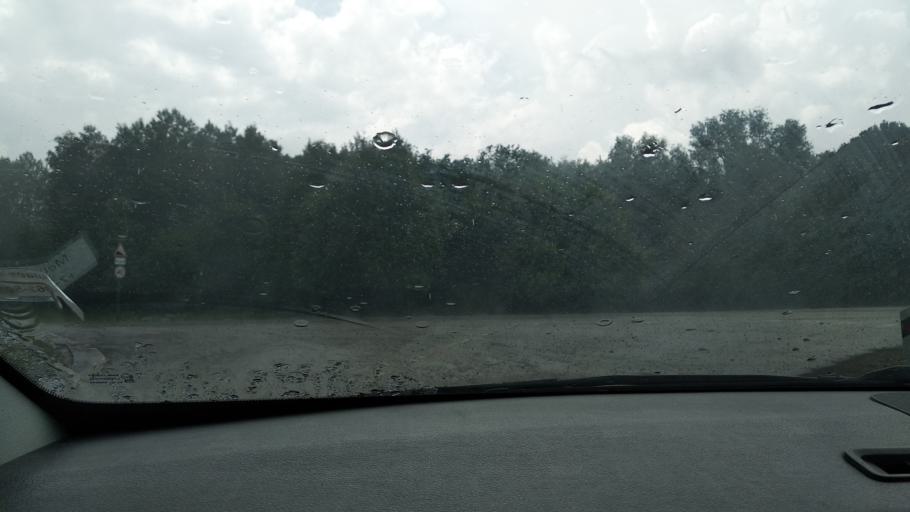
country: RU
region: Adygeya
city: Kamennomostskiy
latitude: 44.2220
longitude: 39.9930
